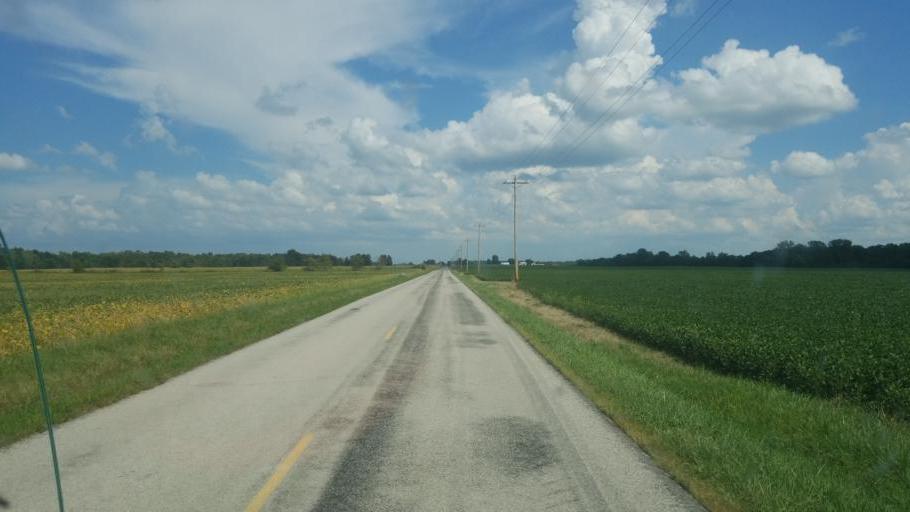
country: US
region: Ohio
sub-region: Seneca County
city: Tiffin
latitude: 40.9936
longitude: -83.0873
